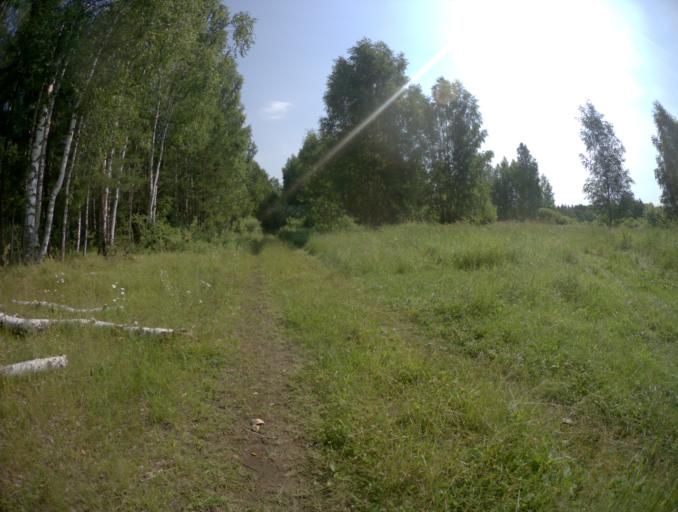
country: RU
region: Vladimir
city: Vyazniki
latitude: 56.3395
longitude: 42.1459
